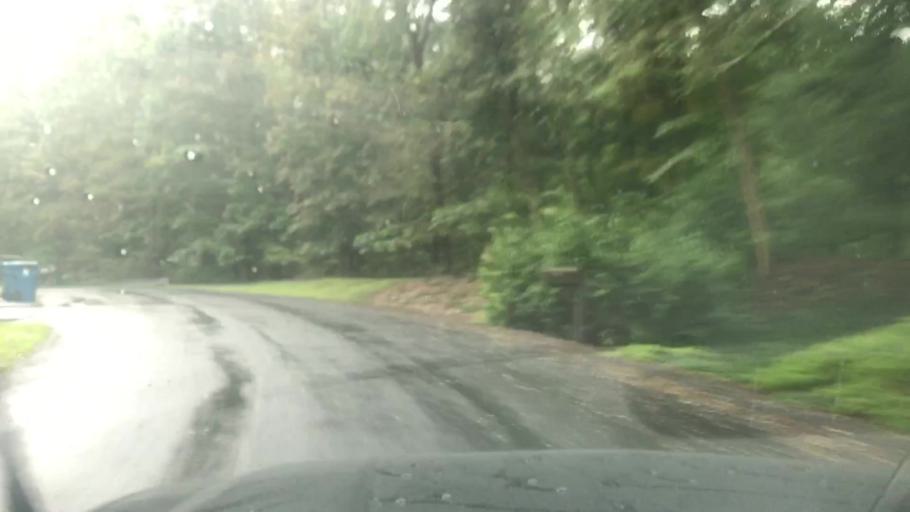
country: US
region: Pennsylvania
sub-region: Cumberland County
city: Shiremanstown
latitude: 40.1784
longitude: -76.9398
